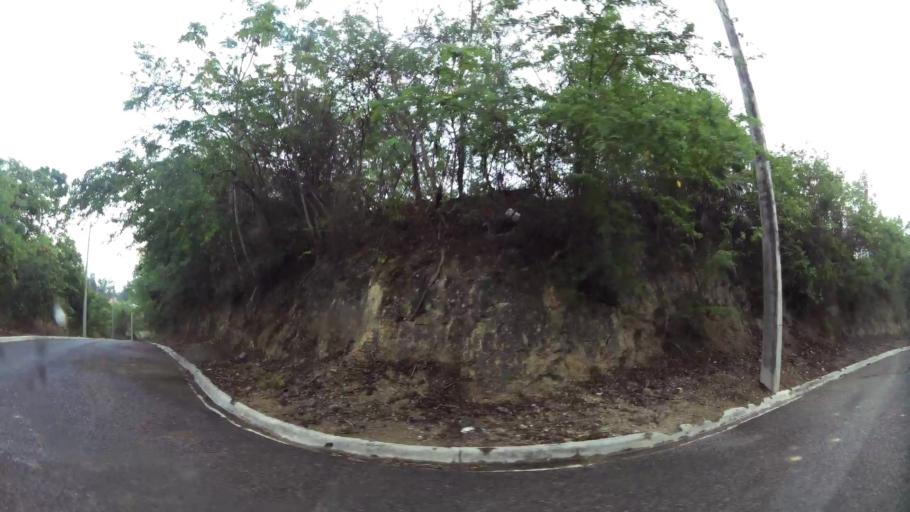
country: DO
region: Nacional
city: La Agustina
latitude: 18.5130
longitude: -69.9402
